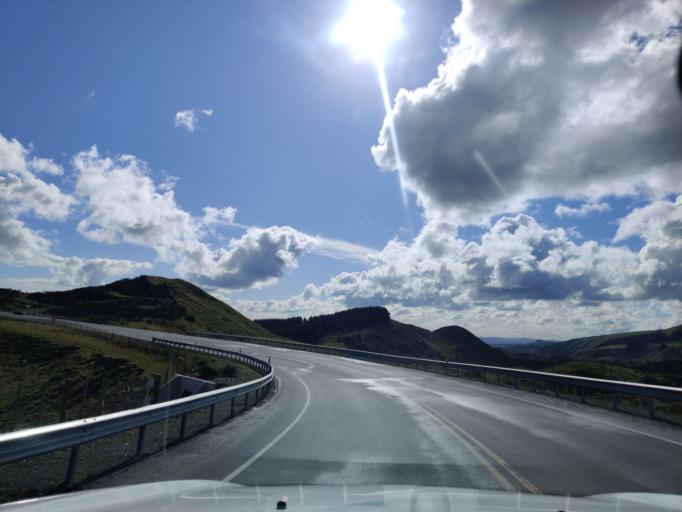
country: NZ
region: Manawatu-Wanganui
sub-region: Palmerston North City
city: Palmerston North
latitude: -40.2924
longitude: 175.8039
